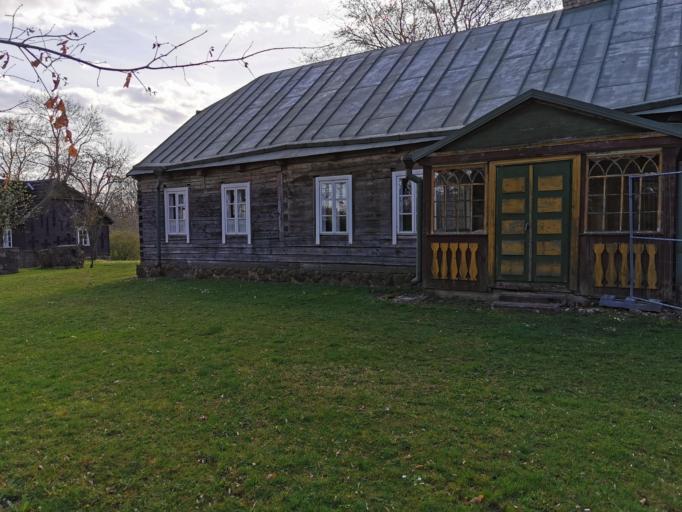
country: LT
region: Kauno apskritis
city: Kedainiai
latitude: 55.5036
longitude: 23.9641
